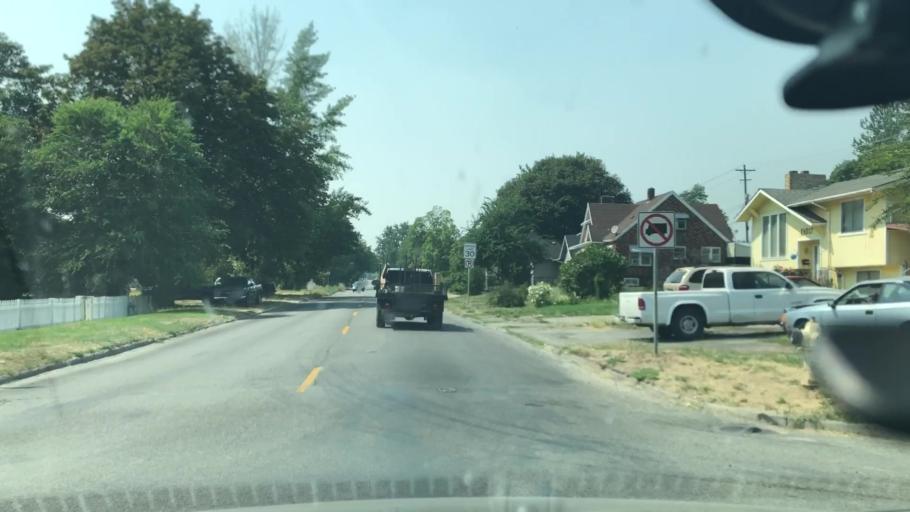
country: US
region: Washington
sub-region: Spokane County
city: Millwood
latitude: 47.6858
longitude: -117.3467
